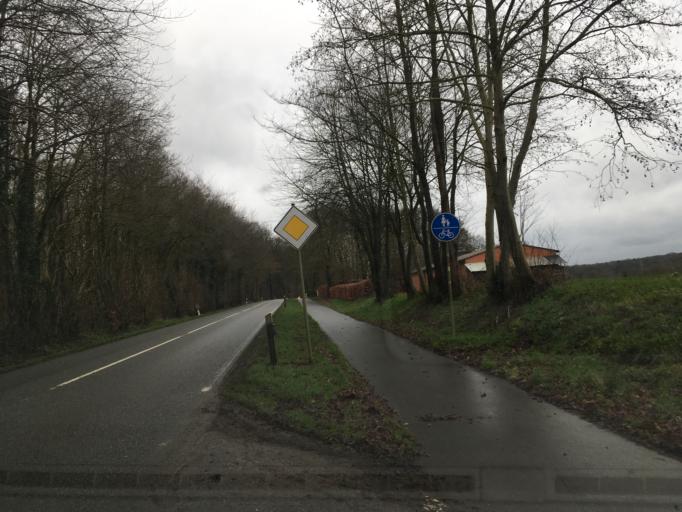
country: DE
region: North Rhine-Westphalia
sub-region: Regierungsbezirk Munster
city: Legden
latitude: 52.0454
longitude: 7.1318
